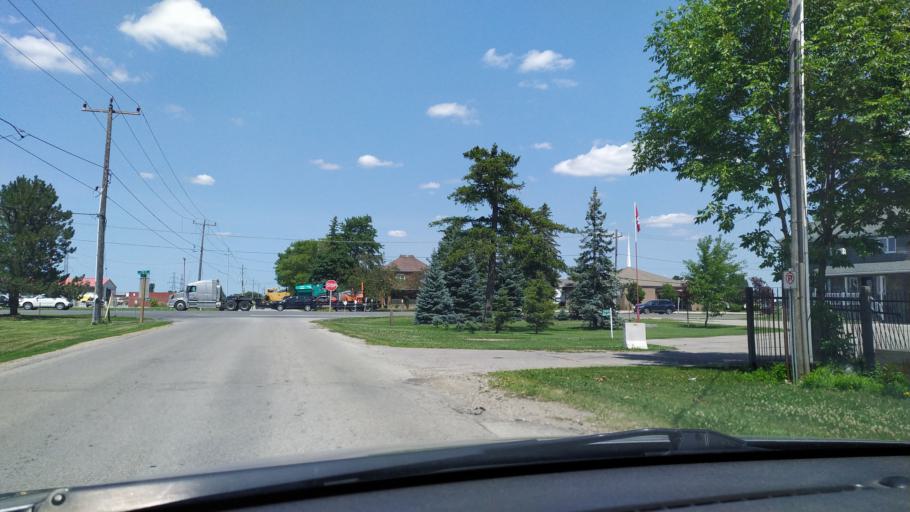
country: CA
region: Ontario
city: Stratford
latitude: 43.3700
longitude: -80.9380
